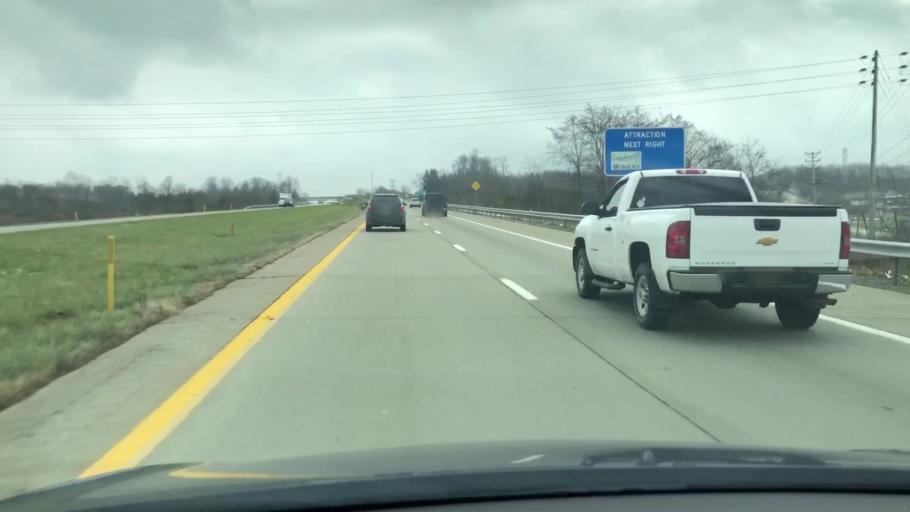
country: US
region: Pennsylvania
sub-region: Westmoreland County
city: Mount Pleasant
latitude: 40.1857
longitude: -79.5678
